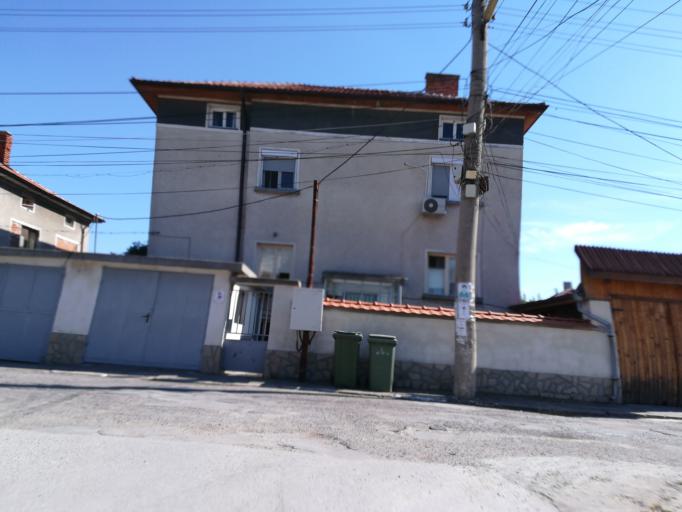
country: BG
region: Stara Zagora
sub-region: Obshtina Chirpan
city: Chirpan
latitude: 42.0937
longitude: 25.2224
